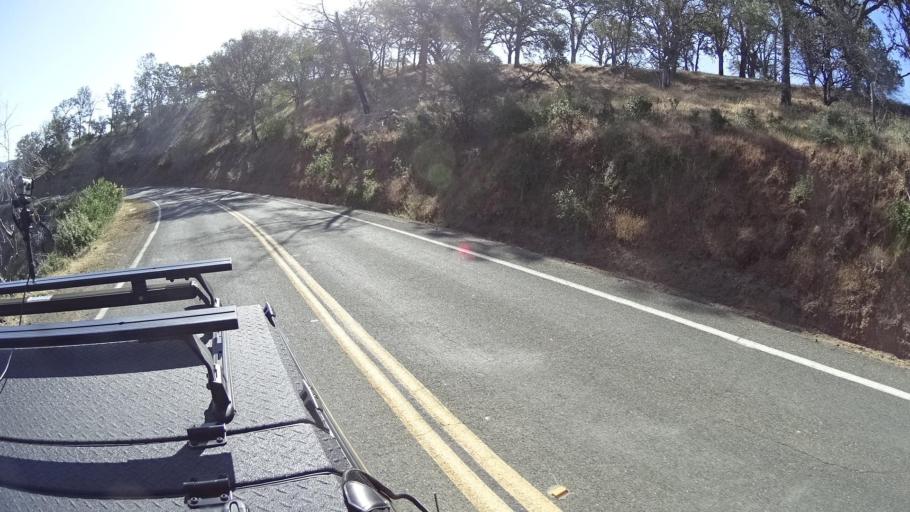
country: US
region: California
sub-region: Lake County
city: Clearlake Oaks
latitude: 38.9948
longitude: -122.6710
